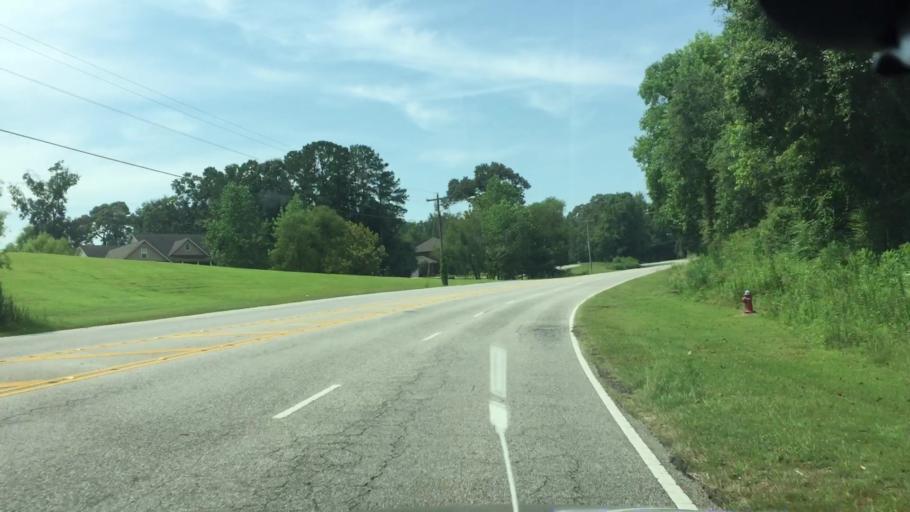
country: US
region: Alabama
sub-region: Coffee County
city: Enterprise
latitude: 31.3536
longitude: -85.8334
